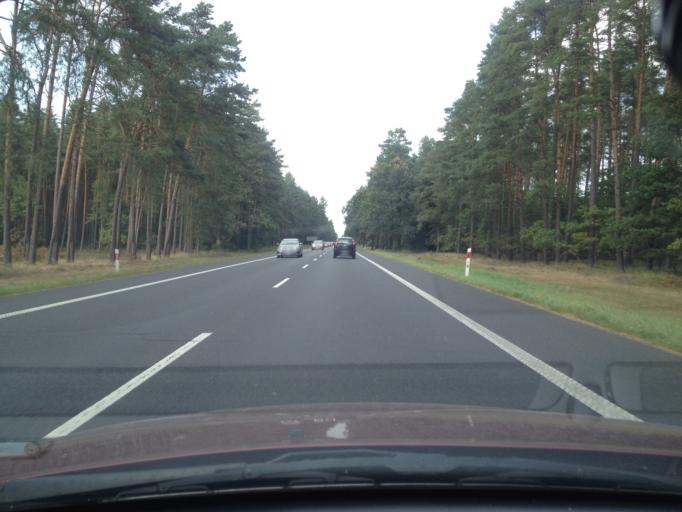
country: PL
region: West Pomeranian Voivodeship
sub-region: Powiat goleniowski
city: Goleniow
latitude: 53.6481
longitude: 14.8164
